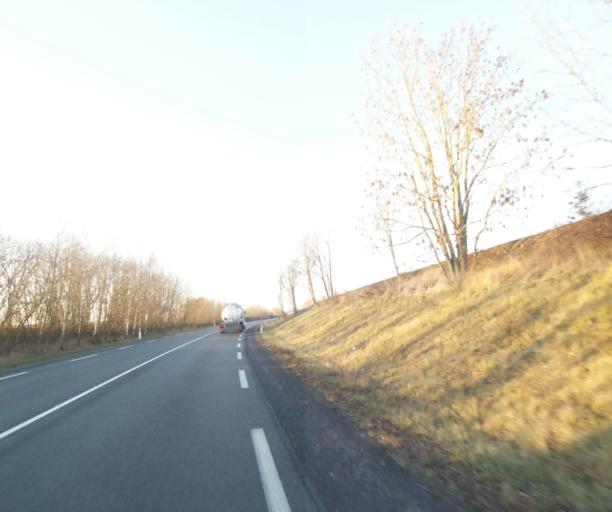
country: FR
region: Champagne-Ardenne
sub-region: Departement de la Haute-Marne
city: Bienville
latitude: 48.5470
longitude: 5.0679
